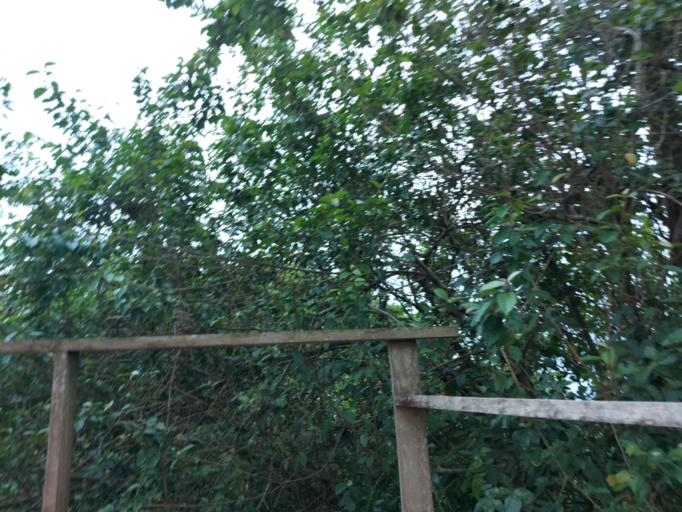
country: PA
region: Bocas del Toro
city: Barranco
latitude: 9.6384
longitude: -82.7805
